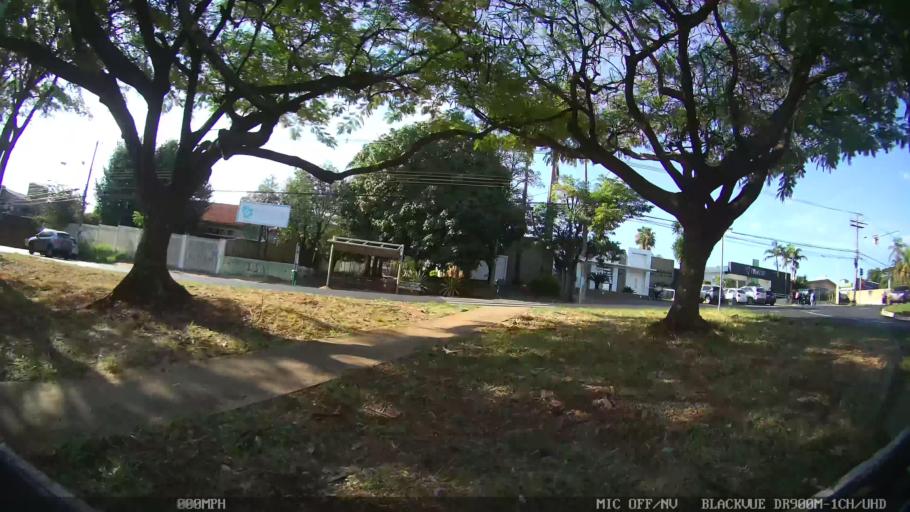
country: BR
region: Sao Paulo
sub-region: Ribeirao Preto
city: Ribeirao Preto
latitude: -21.2013
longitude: -47.7873
